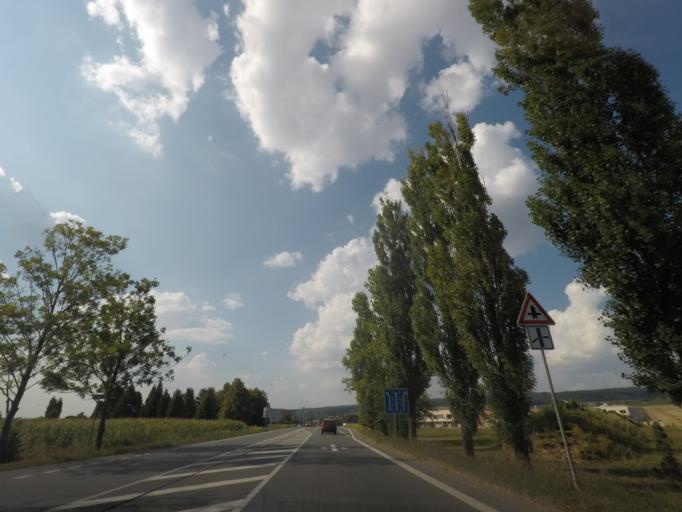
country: CZ
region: Kralovehradecky
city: Dvur Kralove nad Labem
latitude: 50.4189
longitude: 15.8828
